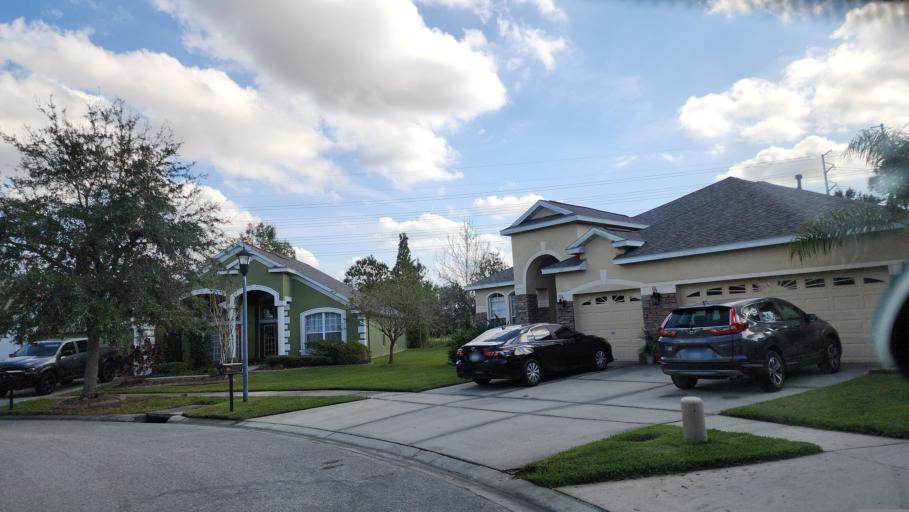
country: US
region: Florida
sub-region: Hillsborough County
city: Fish Hawk
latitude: 27.8388
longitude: -82.2094
